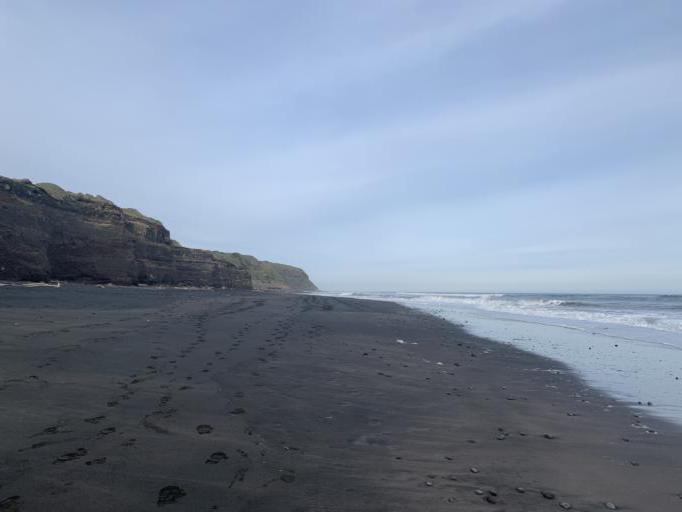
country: NZ
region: Taranaki
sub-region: South Taranaki District
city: Opunake
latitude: -39.5649
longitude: 174.0557
